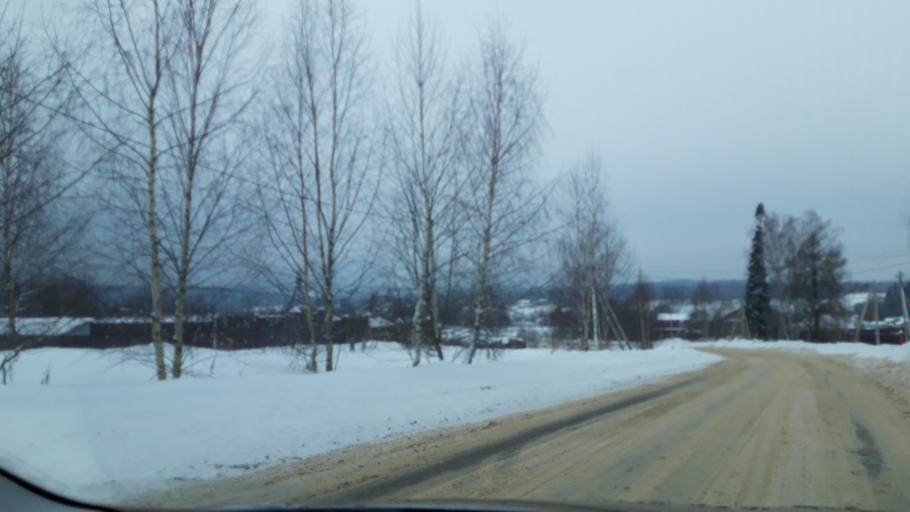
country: RU
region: Moskovskaya
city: Avtopoligon
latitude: 56.2589
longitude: 37.2422
